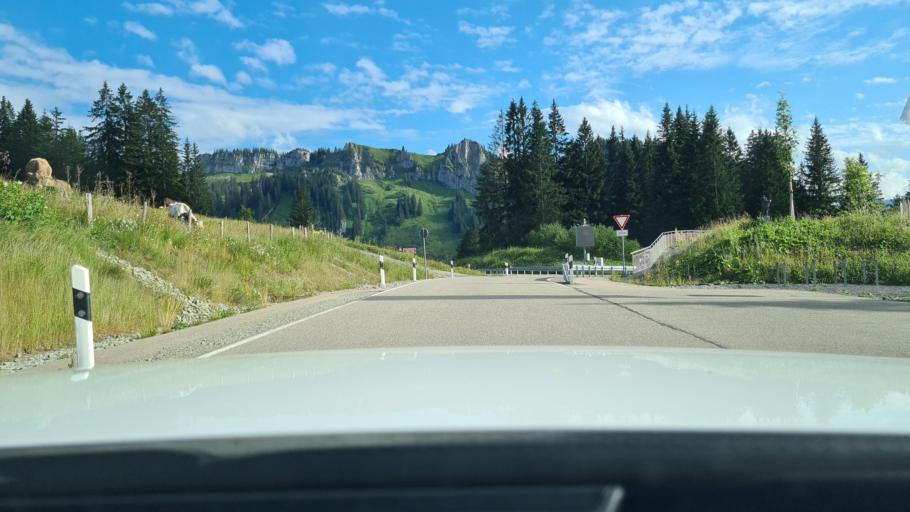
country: DE
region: Bavaria
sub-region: Swabia
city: Obermaiselstein
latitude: 47.4381
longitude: 10.1766
